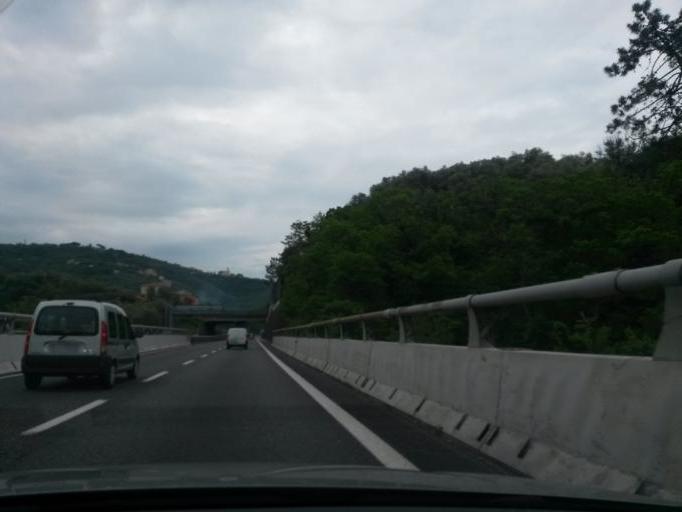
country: IT
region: Liguria
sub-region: Provincia di Genova
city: Lavagna
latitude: 44.3122
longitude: 9.3589
